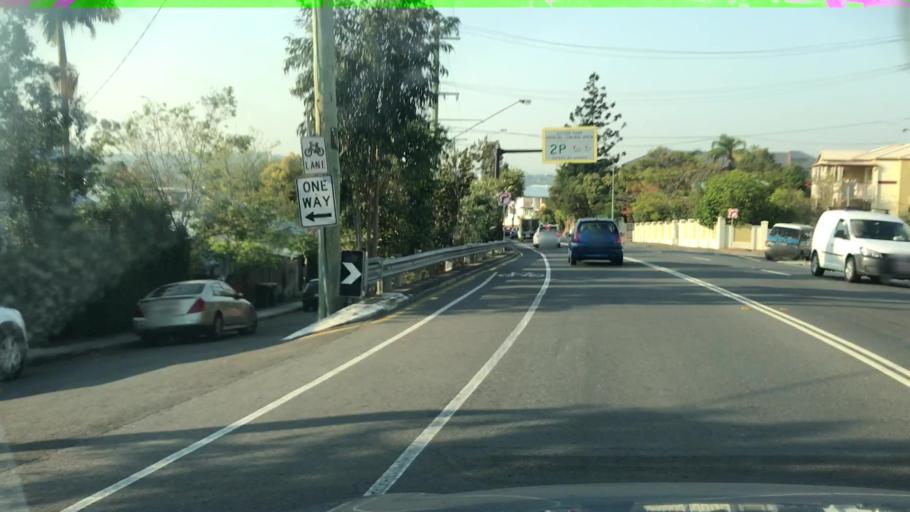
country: AU
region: Queensland
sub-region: Brisbane
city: South Brisbane
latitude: -27.4890
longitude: 153.0186
